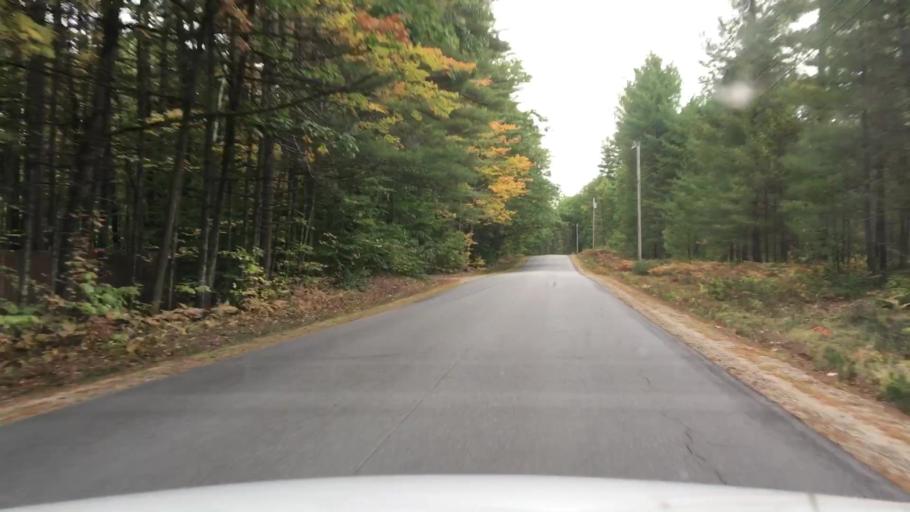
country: US
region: Maine
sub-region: Cumberland County
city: Harrison
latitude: 44.2314
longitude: -70.7054
